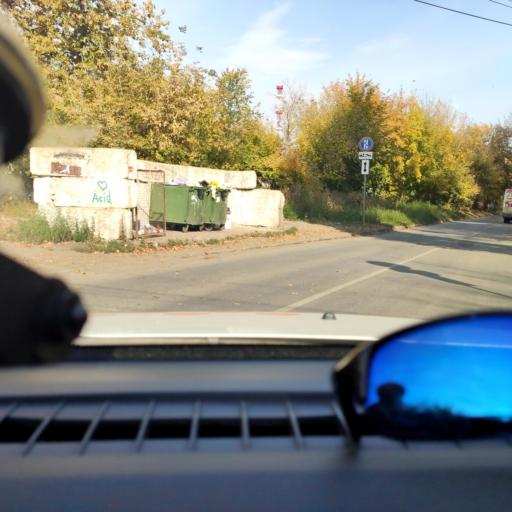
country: RU
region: Samara
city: Samara
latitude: 53.2113
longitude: 50.1821
